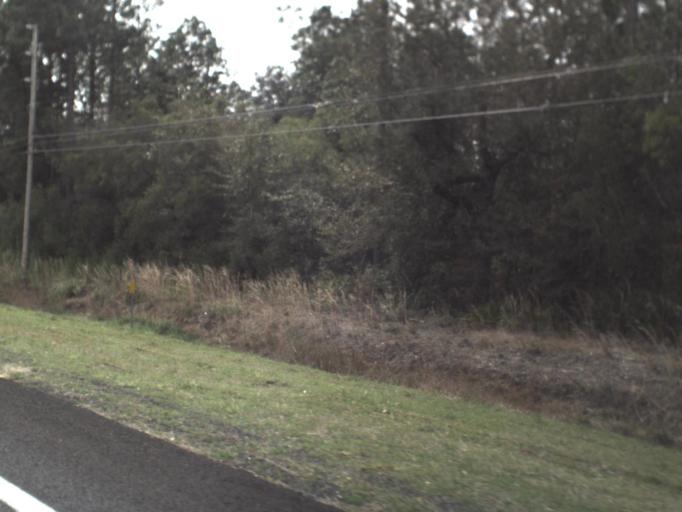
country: US
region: Florida
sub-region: Bay County
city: Youngstown
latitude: 30.4011
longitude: -85.4344
